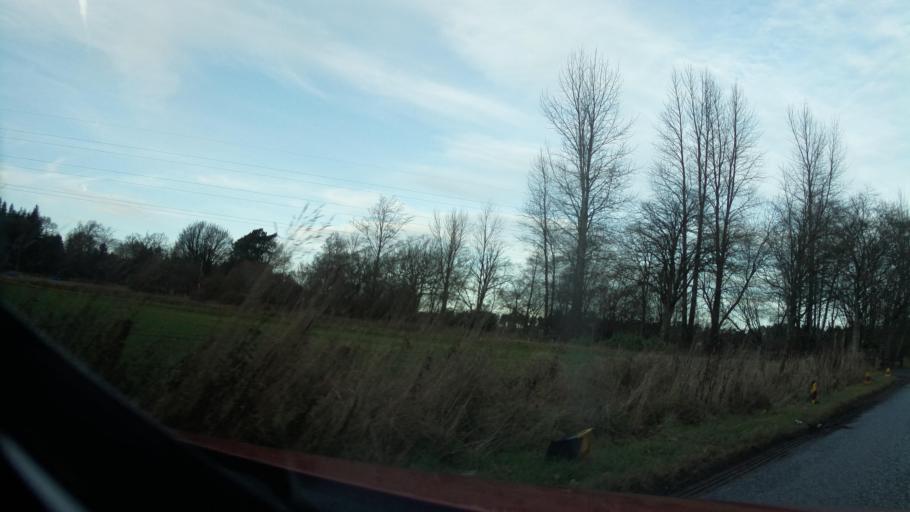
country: GB
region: Scotland
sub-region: Angus
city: Letham
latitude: 56.5487
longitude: -2.7672
